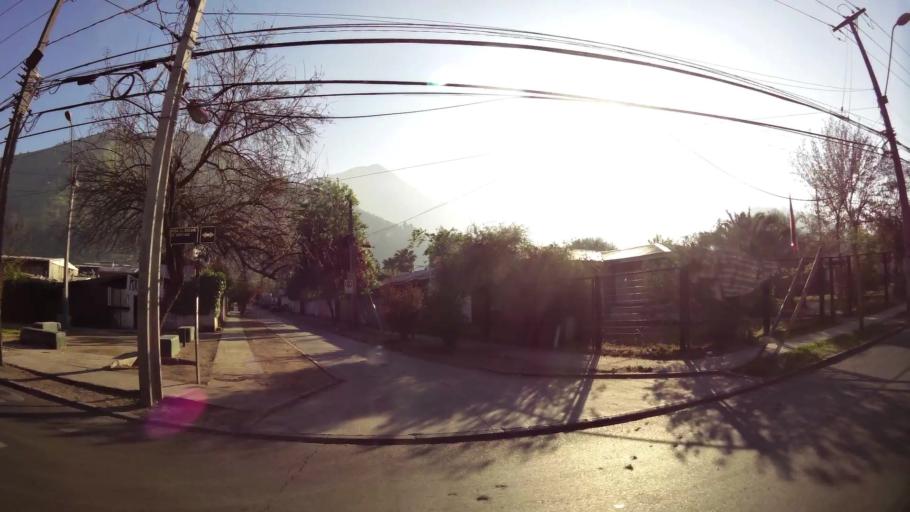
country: CL
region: Santiago Metropolitan
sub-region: Provincia de Santiago
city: Santiago
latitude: -33.3803
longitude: -70.6220
